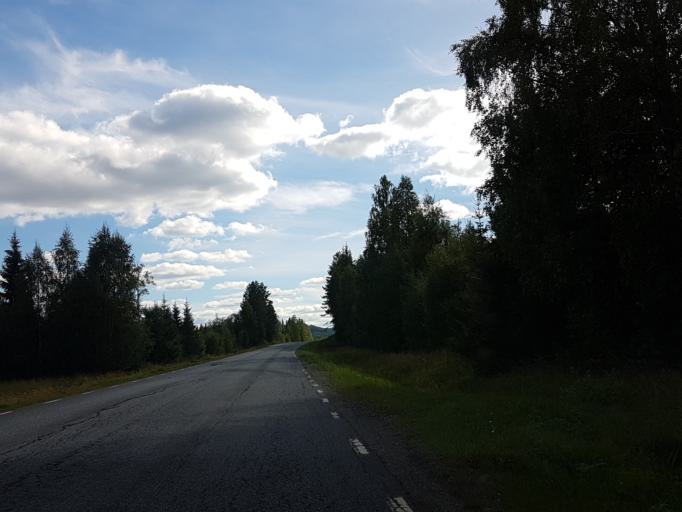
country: SE
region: Vaesterbotten
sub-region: Skelleftea Kommun
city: Burtraesk
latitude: 64.3098
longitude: 20.5315
